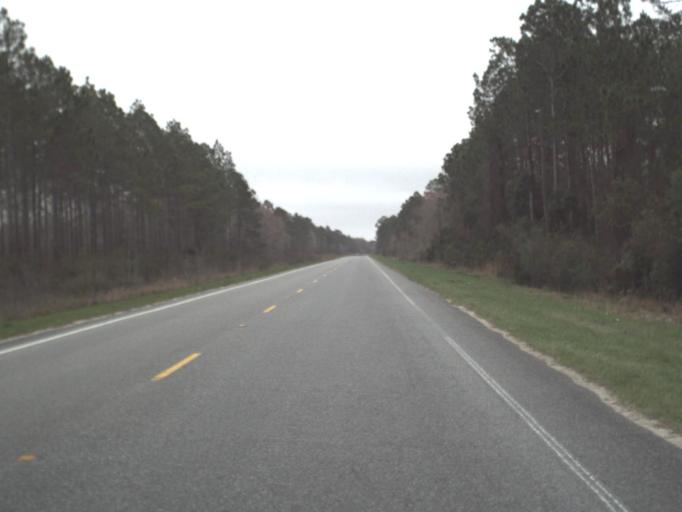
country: US
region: Florida
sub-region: Leon County
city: Woodville
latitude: 30.1924
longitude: -84.1030
